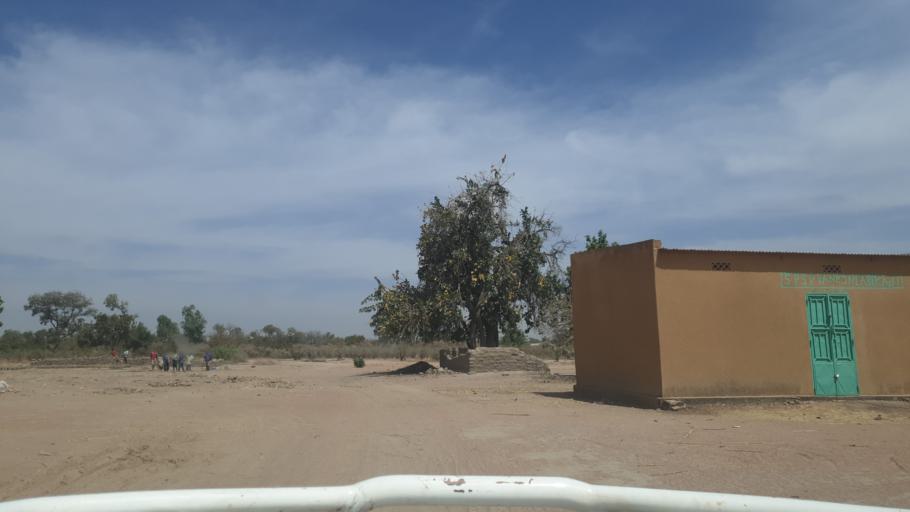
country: ML
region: Sikasso
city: Yorosso
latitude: 12.2787
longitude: -4.6876
